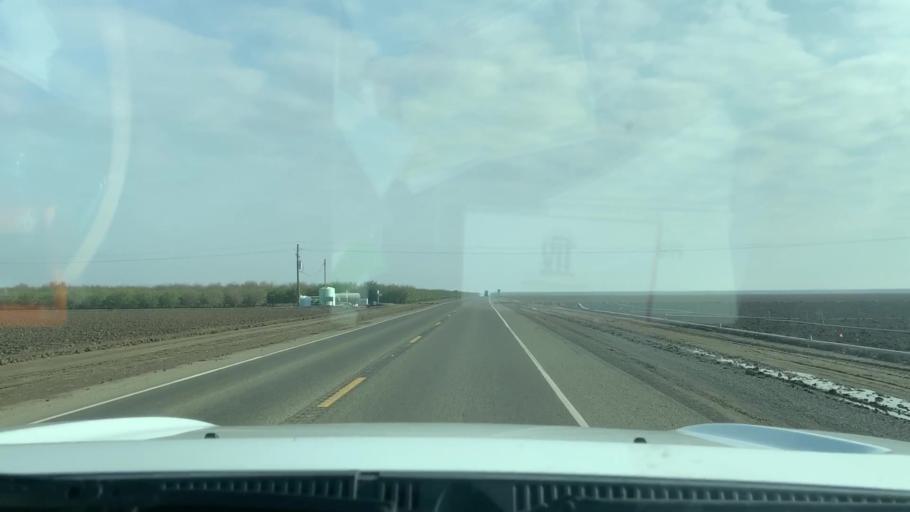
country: US
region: California
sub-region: Fresno County
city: Huron
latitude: 36.2554
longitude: -120.0691
